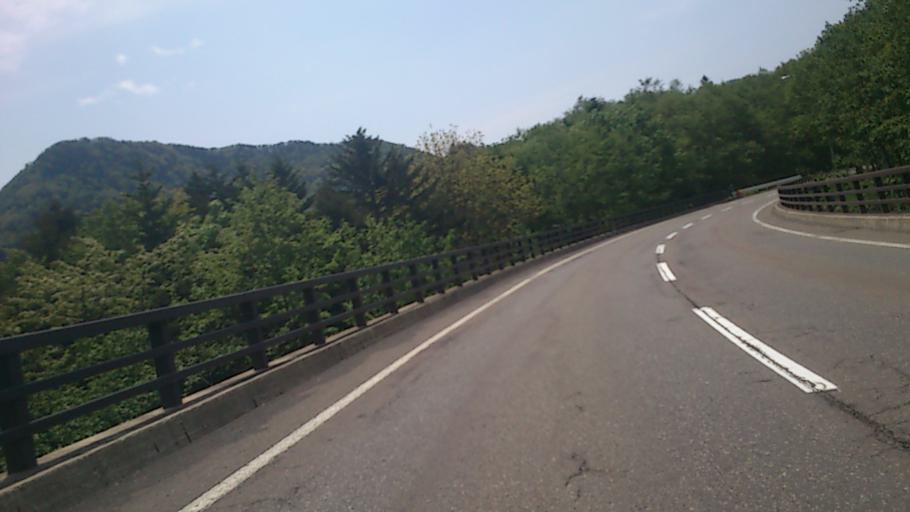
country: JP
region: Hokkaido
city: Otofuke
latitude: 43.3727
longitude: 143.1998
